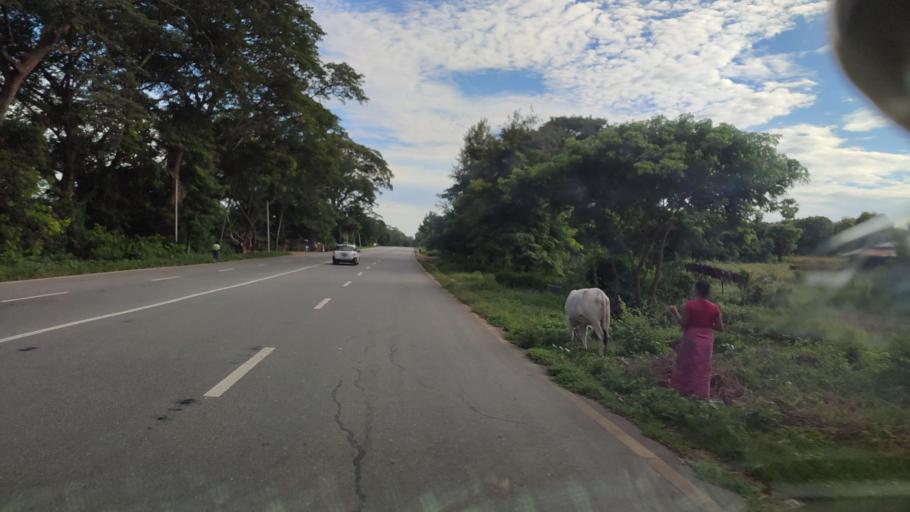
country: MM
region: Mandalay
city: Yamethin
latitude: 20.2142
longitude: 96.1825
